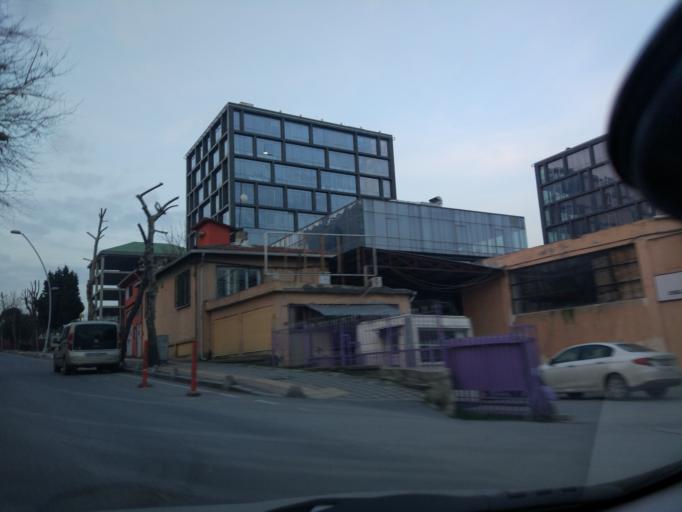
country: TR
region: Istanbul
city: Bahcelievler
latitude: 41.0016
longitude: 28.8222
